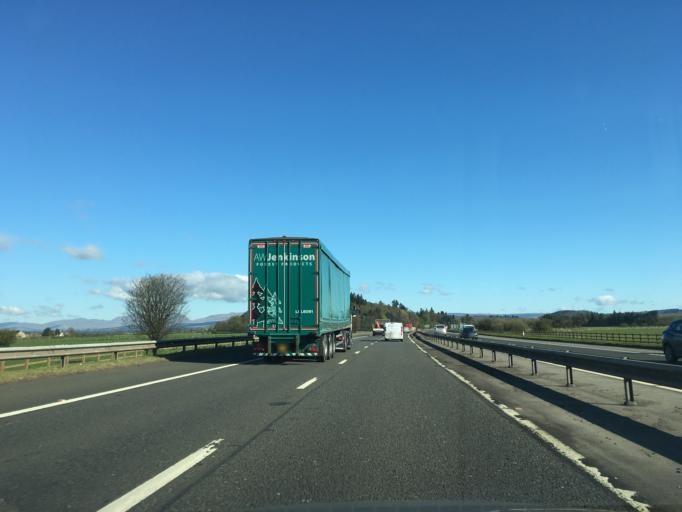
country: GB
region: Scotland
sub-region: Stirling
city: Stirling
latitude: 56.1203
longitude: -3.9697
